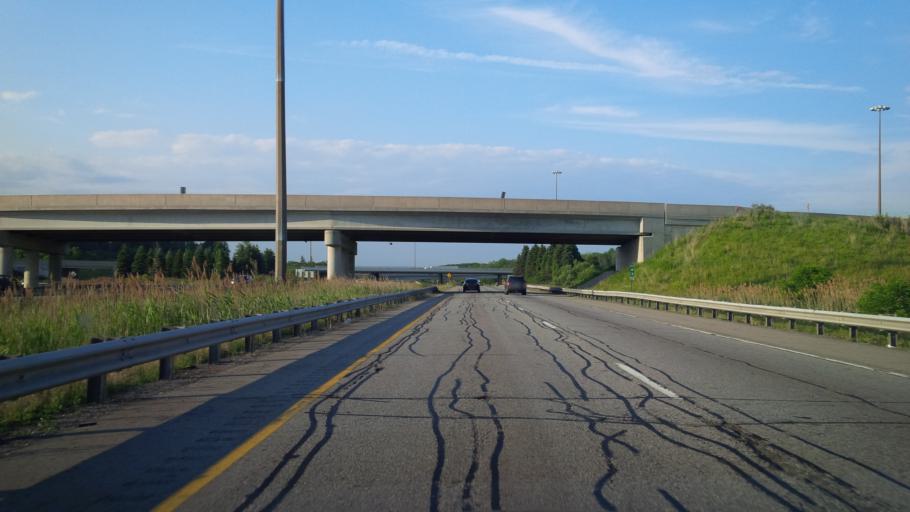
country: CA
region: Ontario
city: Ancaster
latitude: 43.2297
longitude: -79.9530
